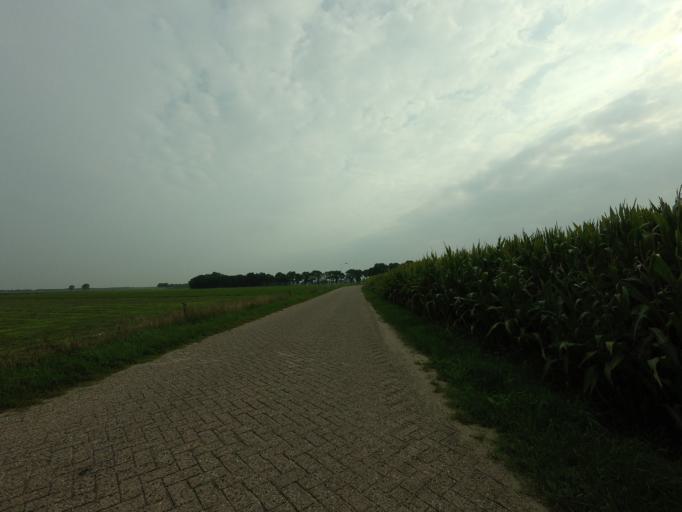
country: NL
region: Drenthe
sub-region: Gemeente Westerveld
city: Dwingeloo
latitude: 52.8697
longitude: 6.4291
